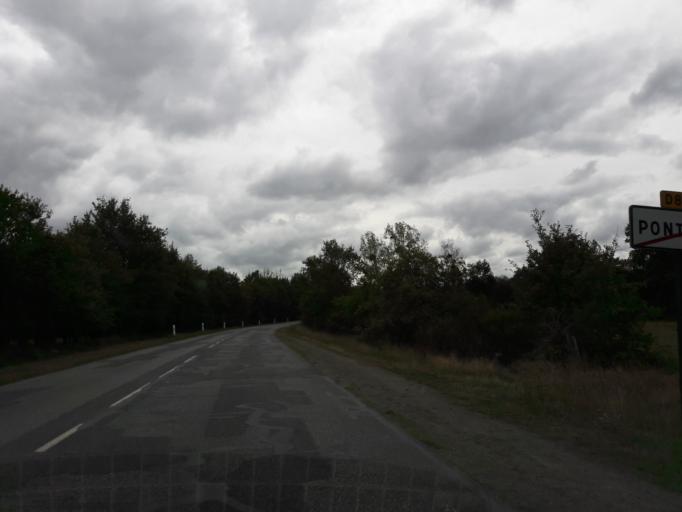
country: FR
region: Brittany
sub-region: Departement d'Ille-et-Vilaine
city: Orgeres
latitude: 48.0040
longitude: -1.6973
